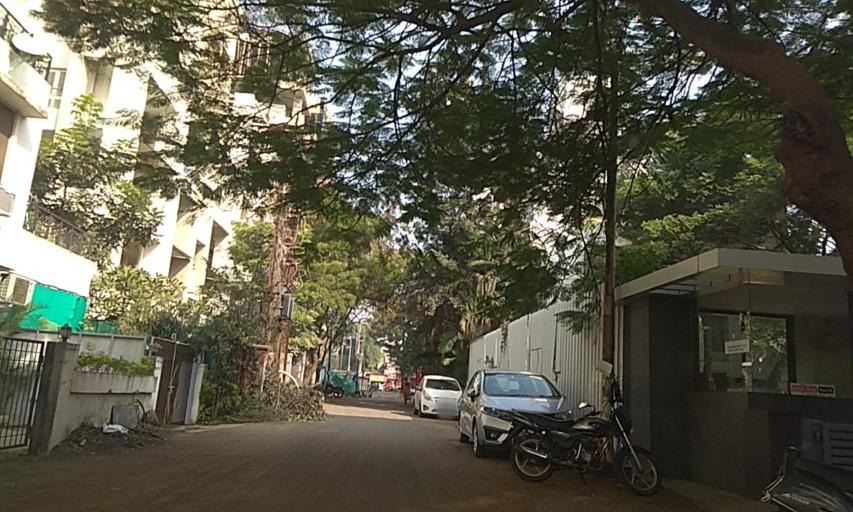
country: IN
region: Maharashtra
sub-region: Pune Division
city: Pimpri
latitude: 18.5632
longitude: 73.7771
